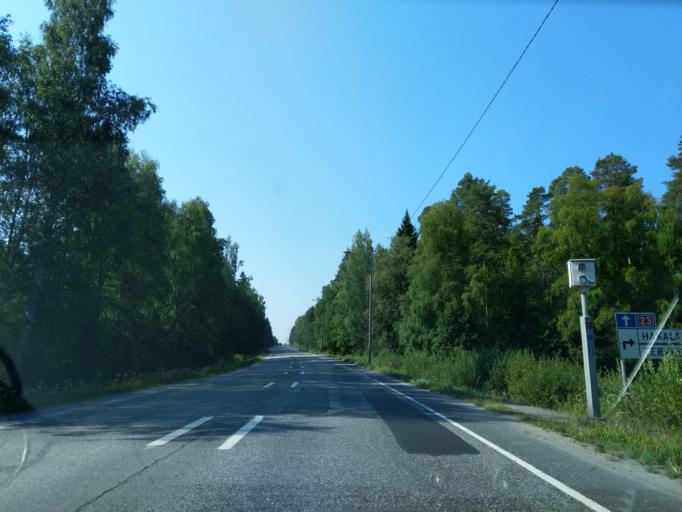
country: FI
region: Satakunta
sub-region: Pori
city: Noormarkku
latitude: 61.5926
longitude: 21.8583
